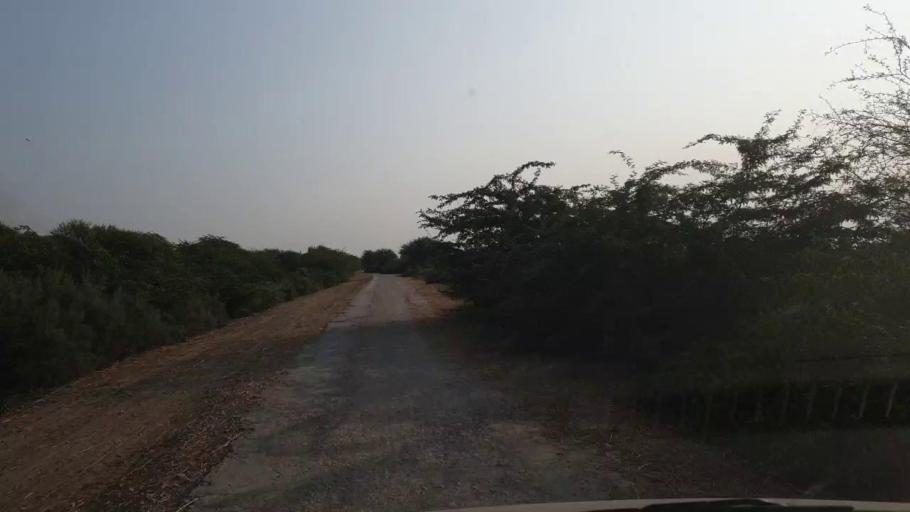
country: PK
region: Sindh
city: Rajo Khanani
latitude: 25.0368
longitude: 68.7771
